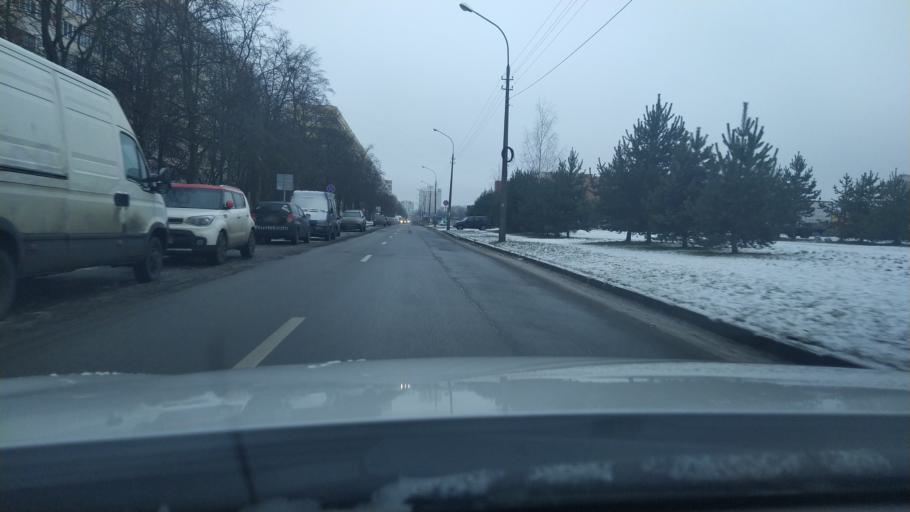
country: RU
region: St.-Petersburg
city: Grazhdanka
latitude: 60.0444
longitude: 30.3944
